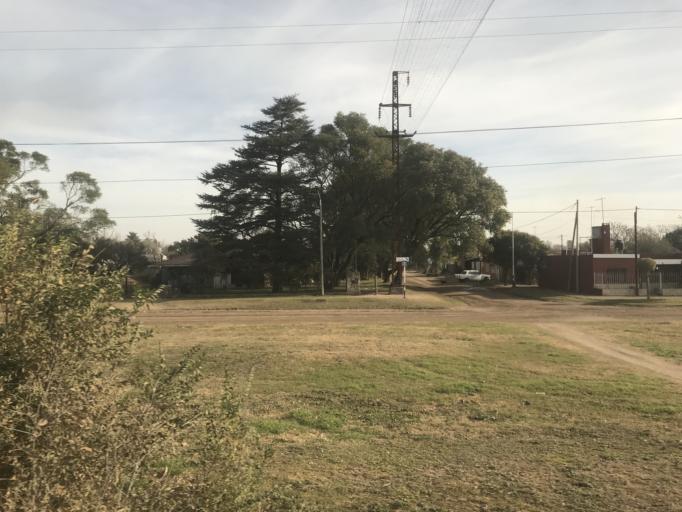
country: AR
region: Cordoba
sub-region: Departamento de Rio Segundo
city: Rio Segundo
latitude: -31.6595
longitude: -63.9054
